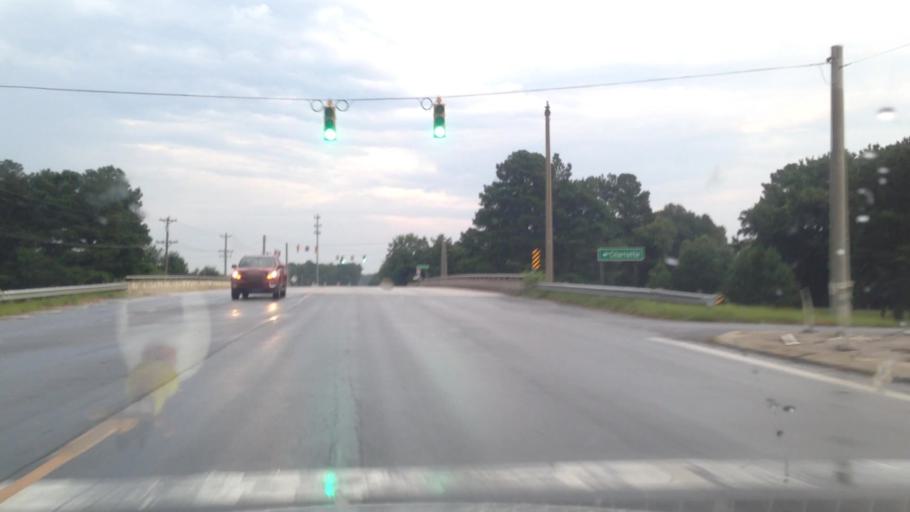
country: US
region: South Carolina
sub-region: York County
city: Fort Mill
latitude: 35.0610
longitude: -80.9572
